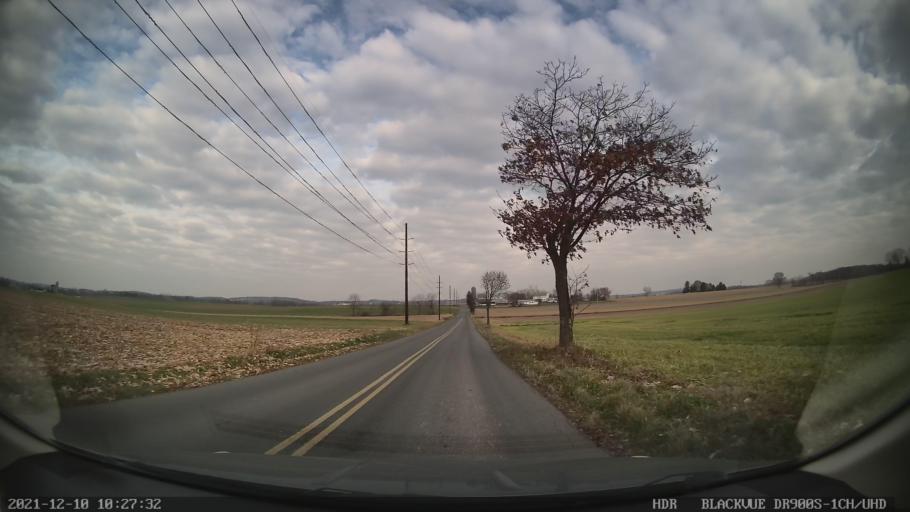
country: US
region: Pennsylvania
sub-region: Berks County
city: Kutztown
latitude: 40.5088
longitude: -75.7466
